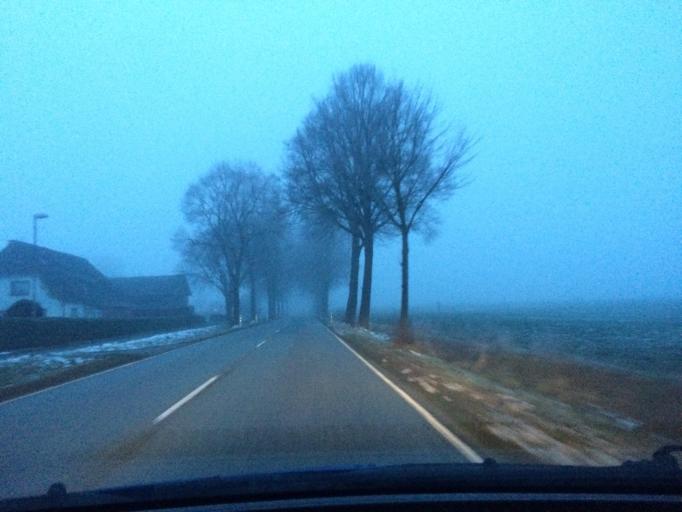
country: DE
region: Schleswig-Holstein
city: Wiershop
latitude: 53.4422
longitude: 10.4457
